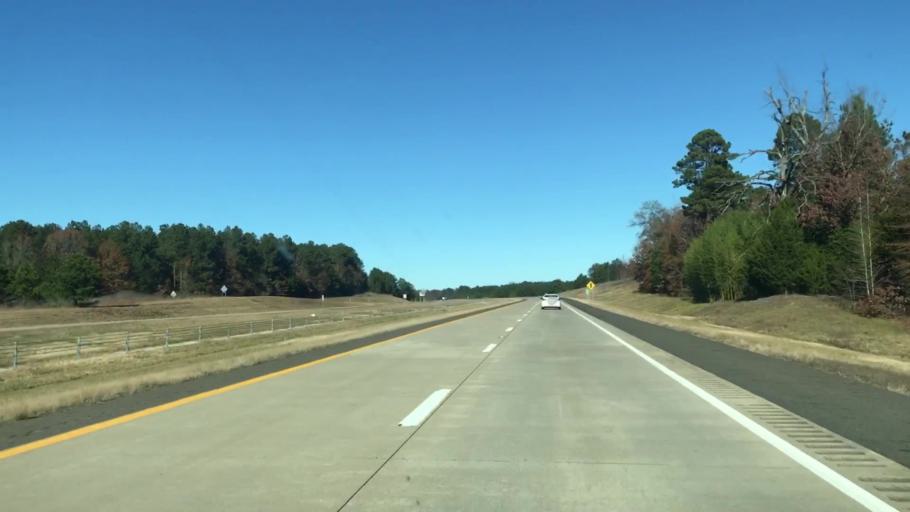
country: US
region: Texas
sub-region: Bowie County
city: Texarkana
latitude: 33.3322
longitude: -93.9605
